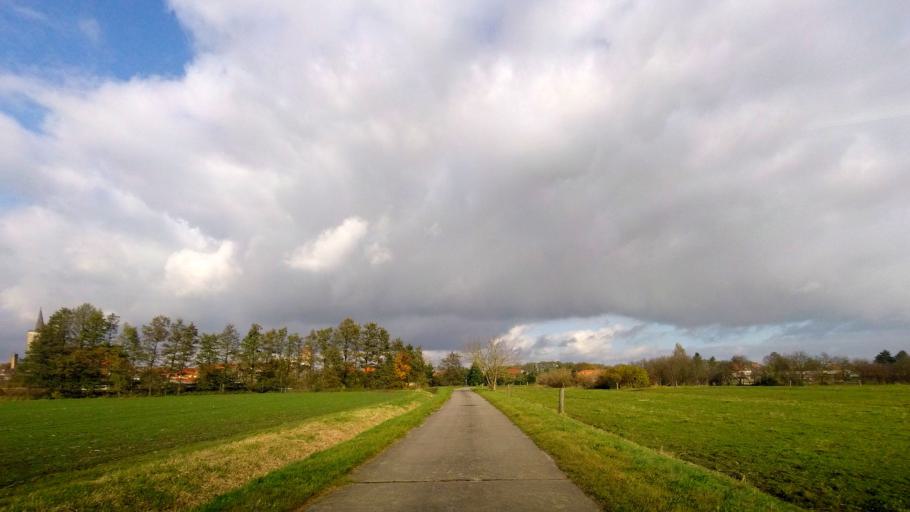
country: DE
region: Brandenburg
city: Juterbog
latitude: 51.9872
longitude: 13.0890
